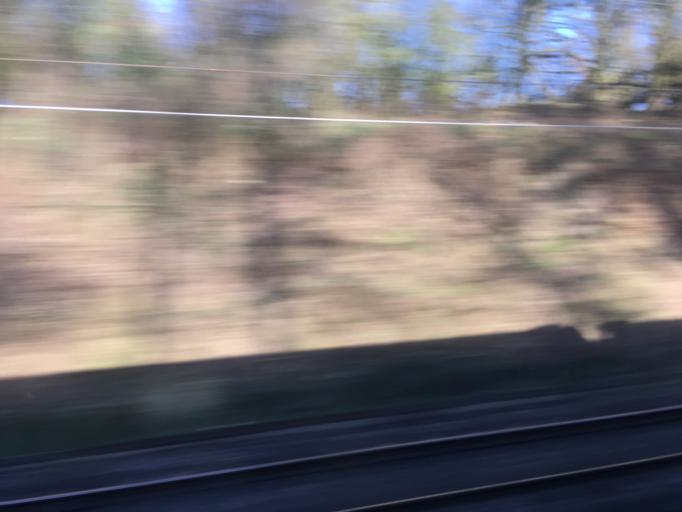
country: GB
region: England
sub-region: Royal Borough of Windsor and Maidenhead
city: White Waltham
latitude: 51.4953
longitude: -0.8014
